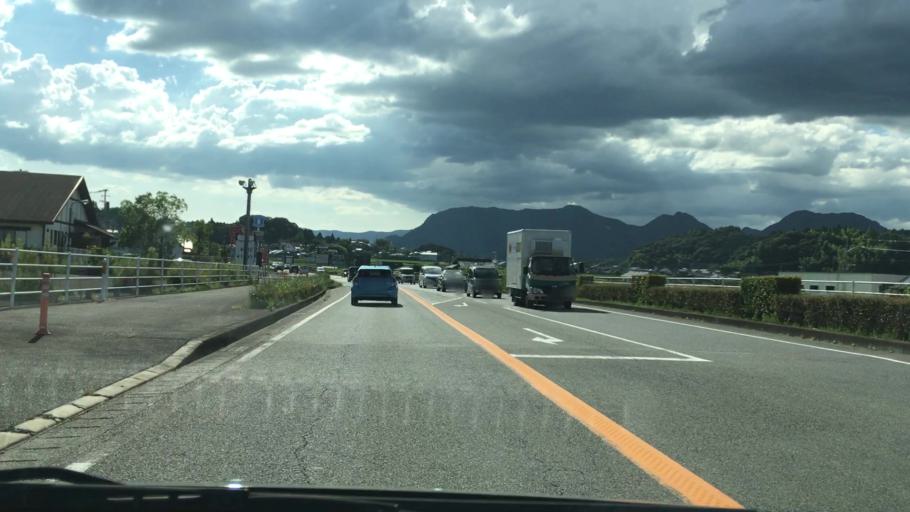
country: JP
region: Saga Prefecture
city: Takeocho-takeo
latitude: 33.1924
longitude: 129.9606
